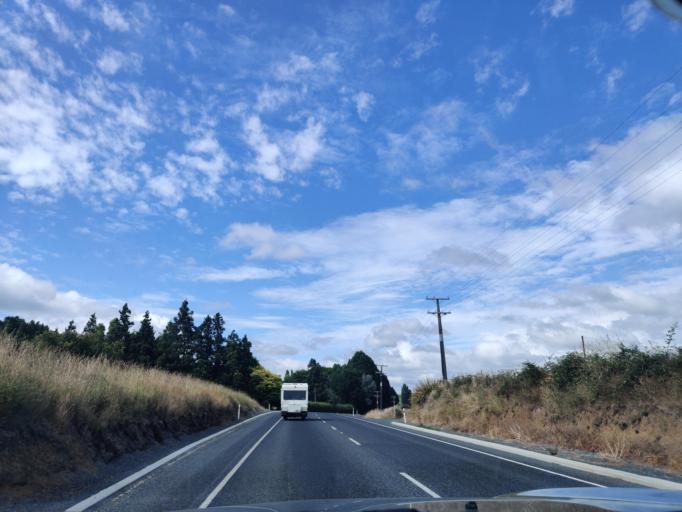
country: NZ
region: Waikato
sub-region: Otorohanga District
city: Otorohanga
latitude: -38.1205
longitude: 175.1977
